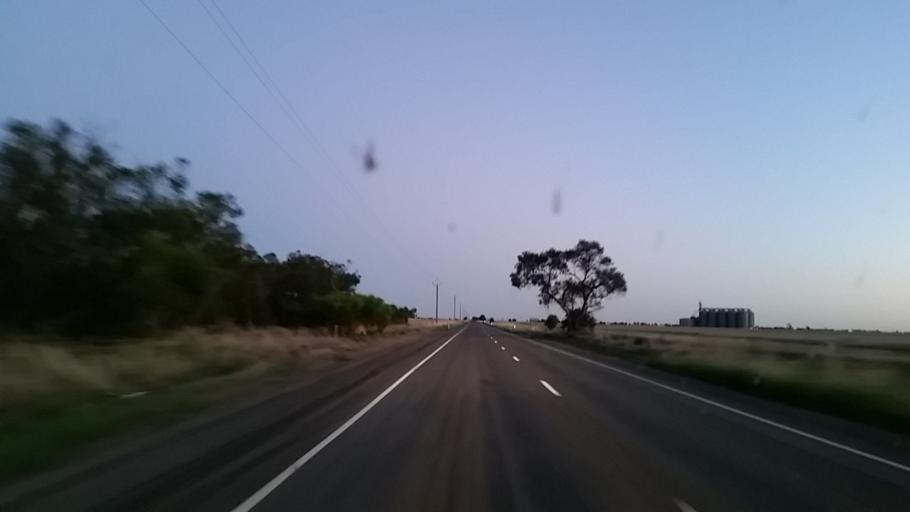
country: AU
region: South Australia
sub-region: Wakefield
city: Balaklava
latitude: -34.1683
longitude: 138.4300
